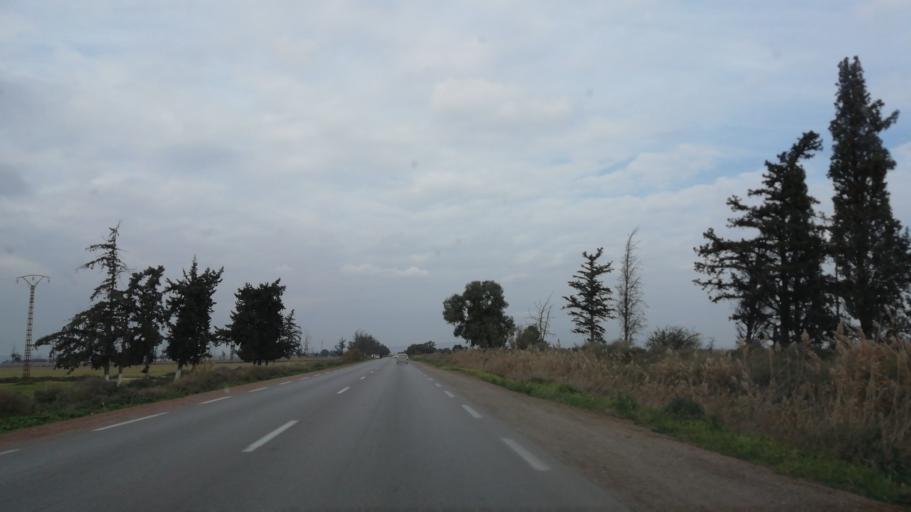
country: DZ
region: Mostaganem
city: Mostaganem
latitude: 35.6726
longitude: 0.0576
